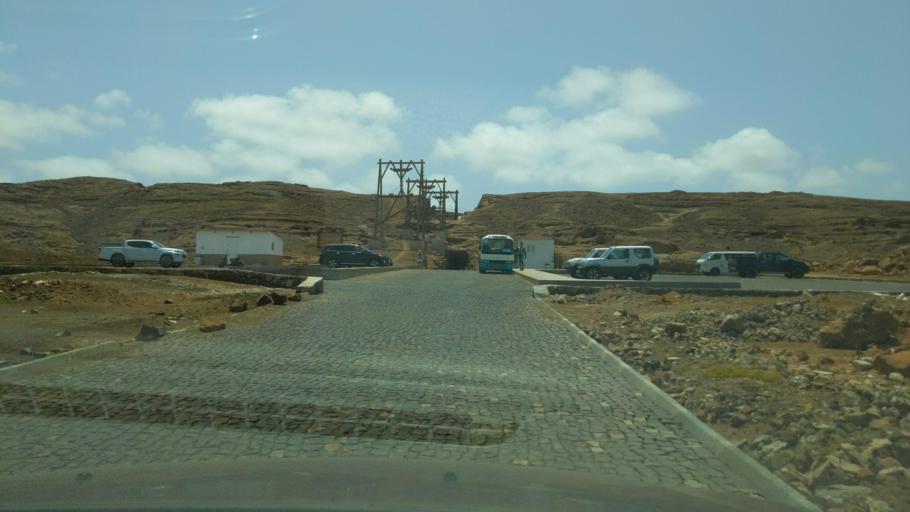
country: CV
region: Sal
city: Espargos
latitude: 16.7679
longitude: -22.8958
